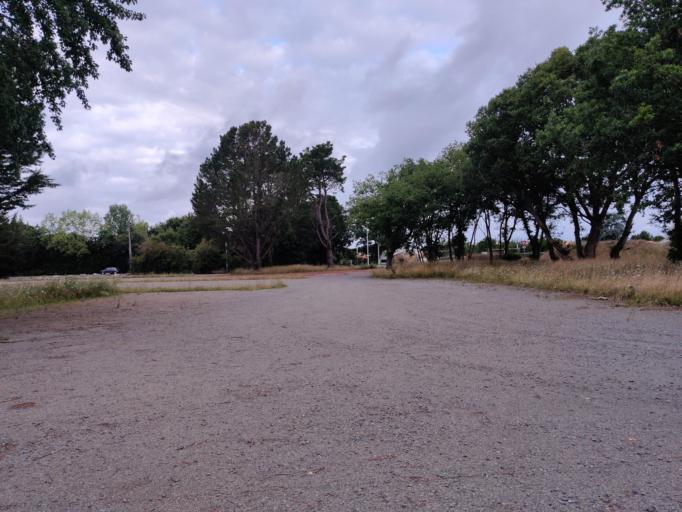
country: FR
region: Pays de la Loire
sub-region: Departement de la Vendee
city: Chateau-d'Olonne
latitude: 46.5186
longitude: -1.7559
